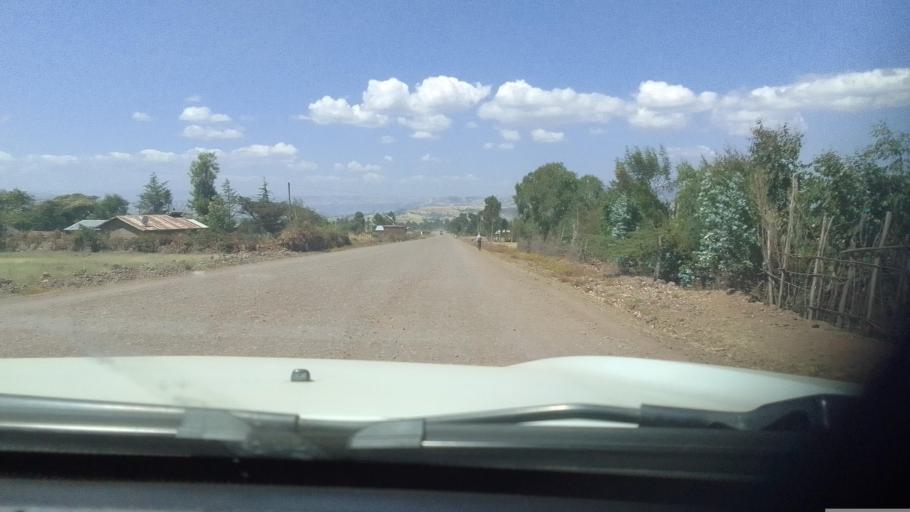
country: ET
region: Oromiya
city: Hagere Hiywet
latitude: 8.9274
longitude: 37.8607
